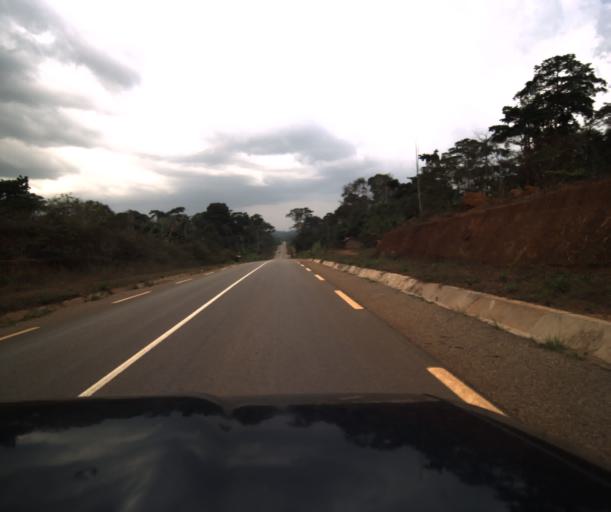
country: CM
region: Centre
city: Akono
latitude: 3.6279
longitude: 11.3224
